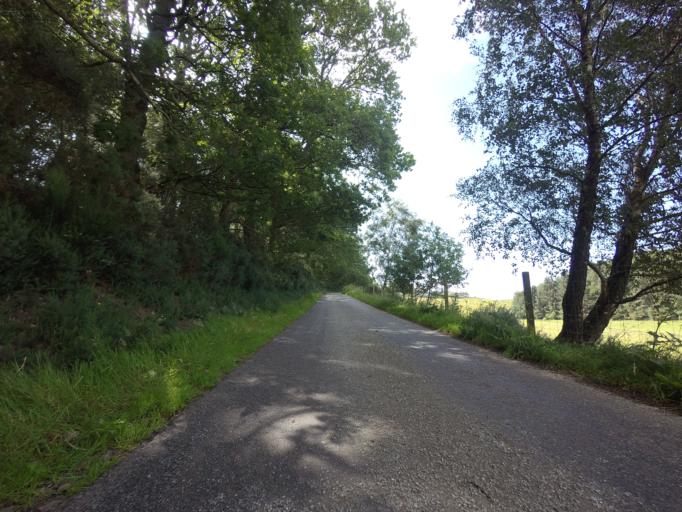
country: GB
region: Scotland
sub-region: Highland
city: Nairn
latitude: 57.5416
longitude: -3.8664
